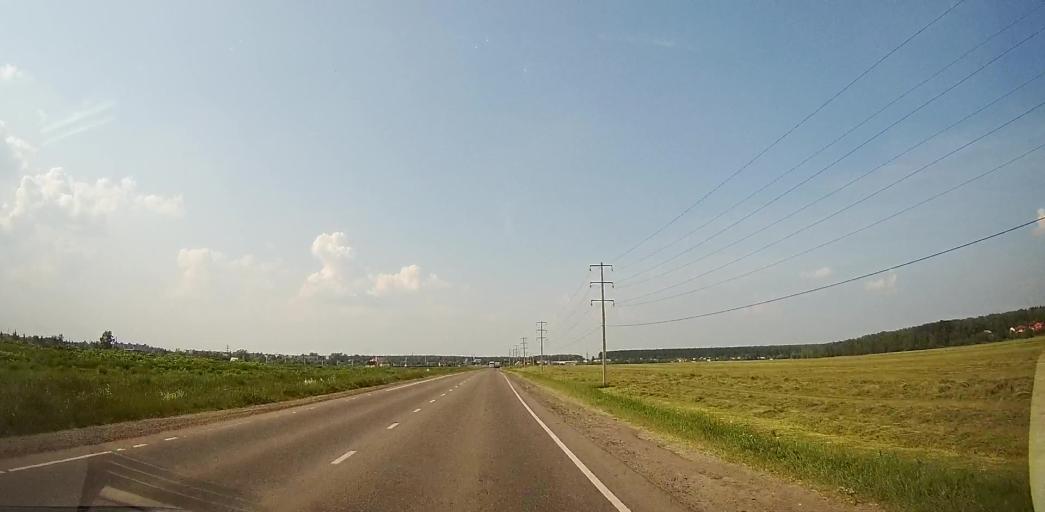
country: RU
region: Moskovskaya
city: Barybino
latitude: 55.2649
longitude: 37.9168
